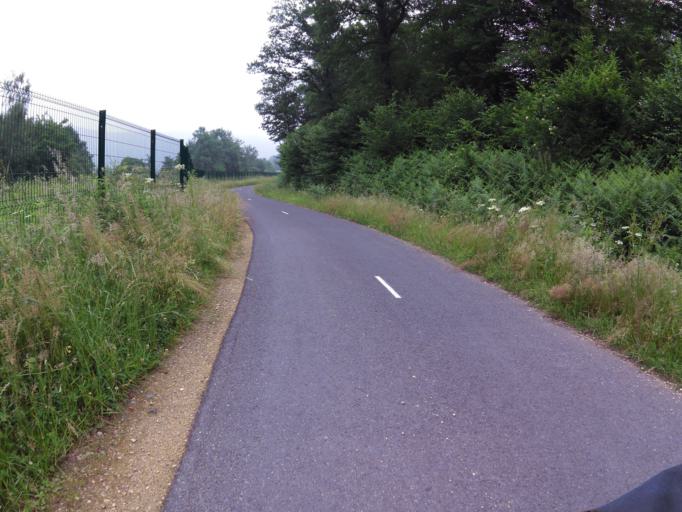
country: FR
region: Champagne-Ardenne
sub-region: Departement des Ardennes
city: Revin
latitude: 49.9624
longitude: 4.6616
